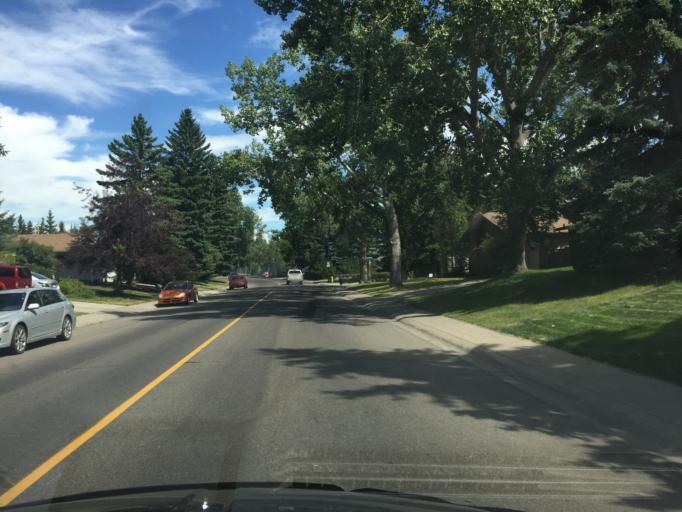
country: CA
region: Alberta
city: Calgary
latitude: 50.9455
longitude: -114.0552
